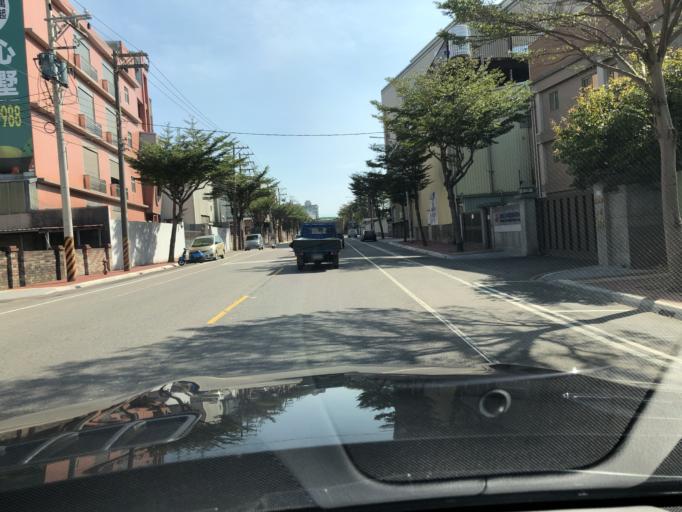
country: TW
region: Taiwan
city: Taoyuan City
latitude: 25.0731
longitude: 121.2875
